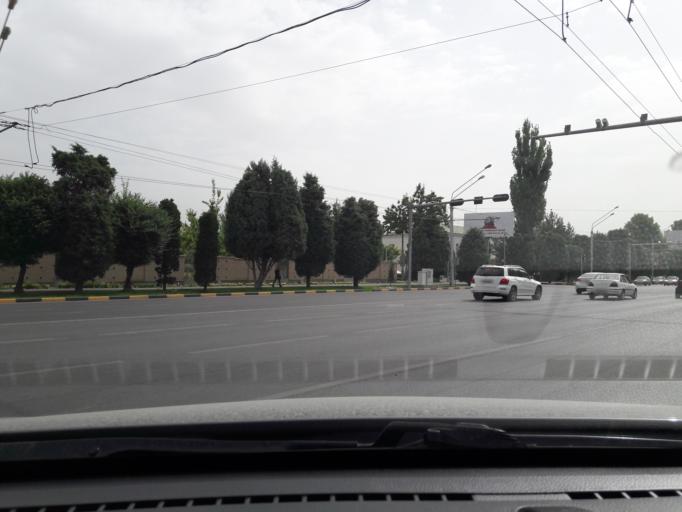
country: TJ
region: Dushanbe
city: Dushanbe
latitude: 38.5838
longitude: 68.7640
